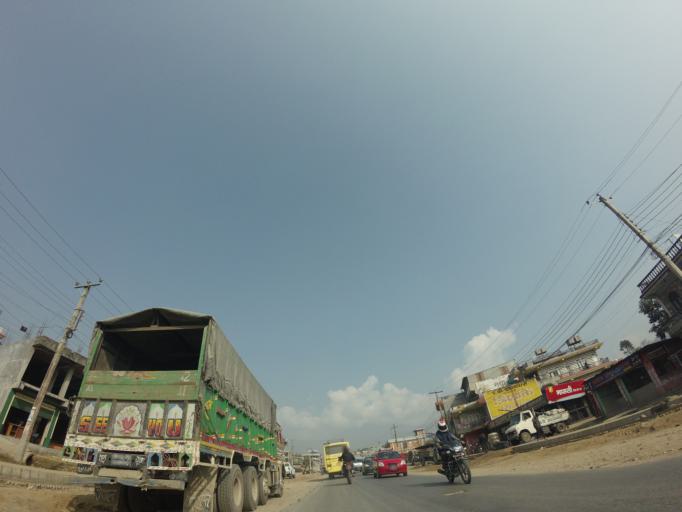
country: NP
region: Western Region
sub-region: Gandaki Zone
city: Pokhara
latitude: 28.2330
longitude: 83.9827
